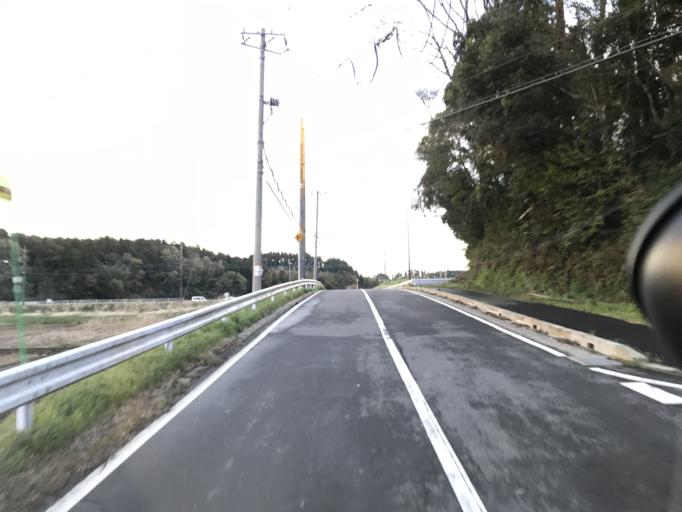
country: JP
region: Chiba
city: Sawara
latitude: 35.8152
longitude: 140.4927
